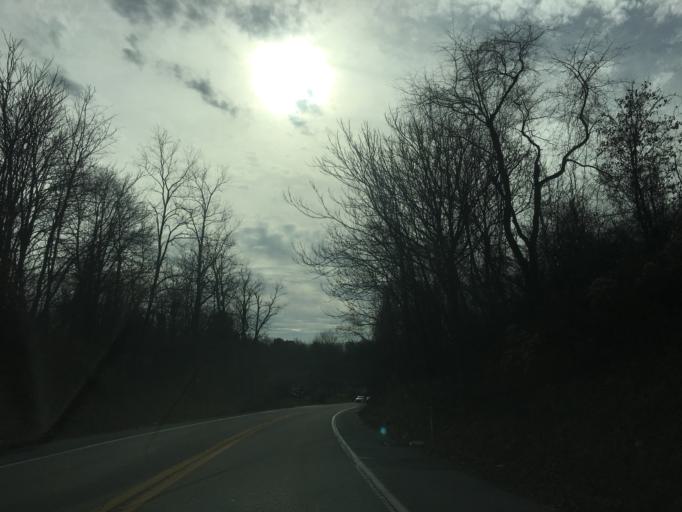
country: US
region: Pennsylvania
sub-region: Dauphin County
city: Colonial Park
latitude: 40.3136
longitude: -76.8219
